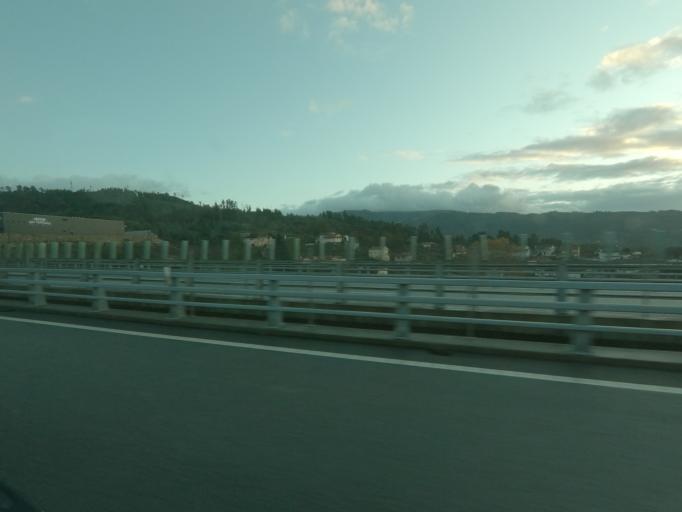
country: PT
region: Porto
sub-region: Amarante
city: Amarante
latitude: 41.2616
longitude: -8.0233
